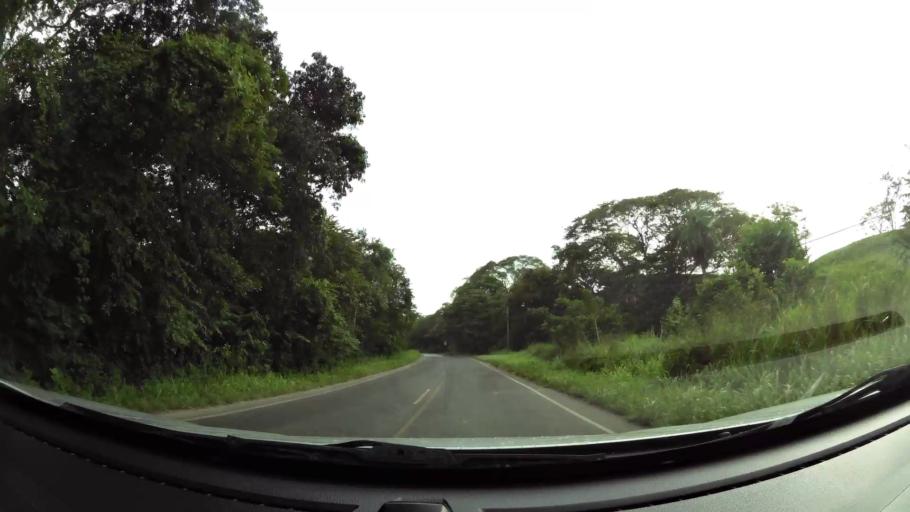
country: CR
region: Guanacaste
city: Juntas
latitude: 10.2009
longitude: -84.9581
